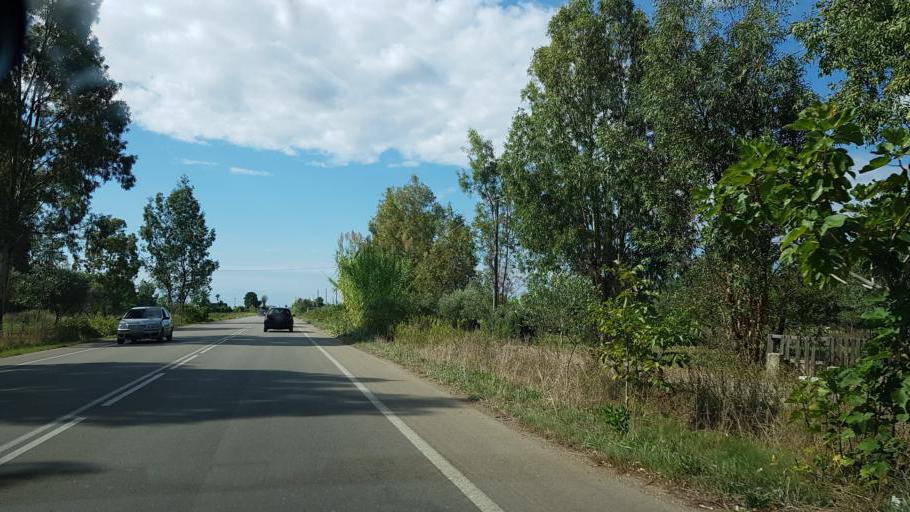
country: IT
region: Apulia
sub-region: Provincia di Lecce
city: Leverano
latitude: 40.3072
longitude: 18.0168
